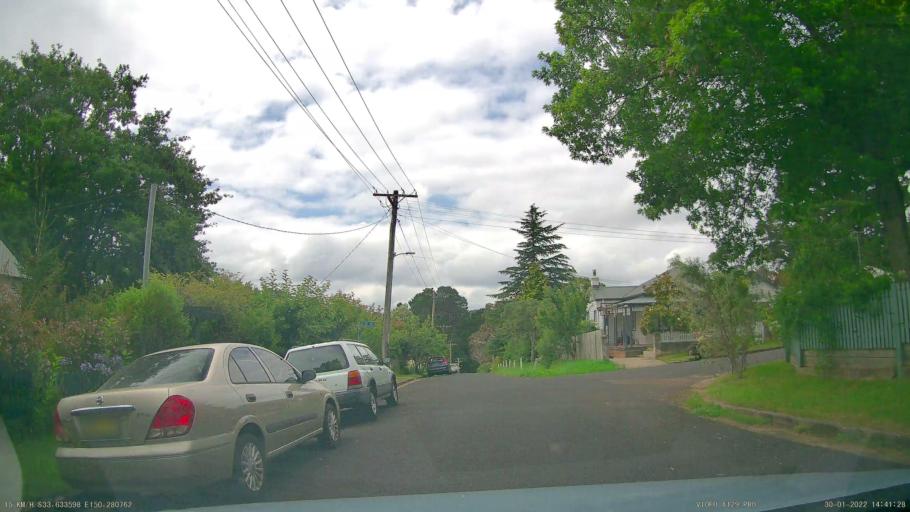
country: AU
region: New South Wales
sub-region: Blue Mountains Municipality
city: Blackheath
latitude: -33.6335
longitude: 150.2807
